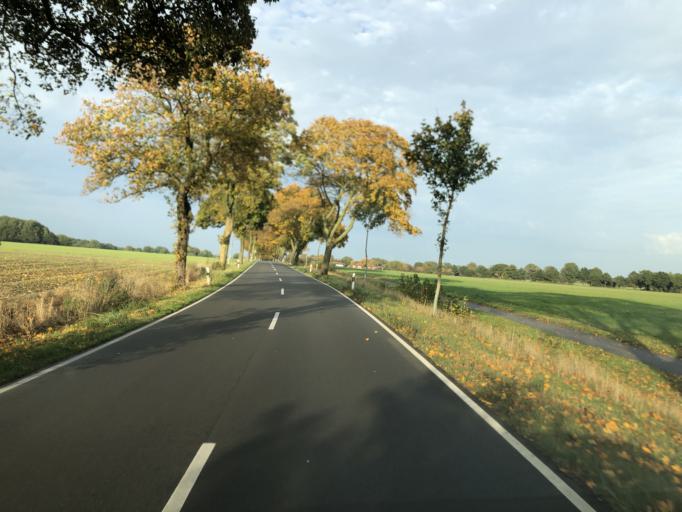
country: DE
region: Lower Saxony
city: Neu Wulmstorf
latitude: 53.4305
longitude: 9.7970
